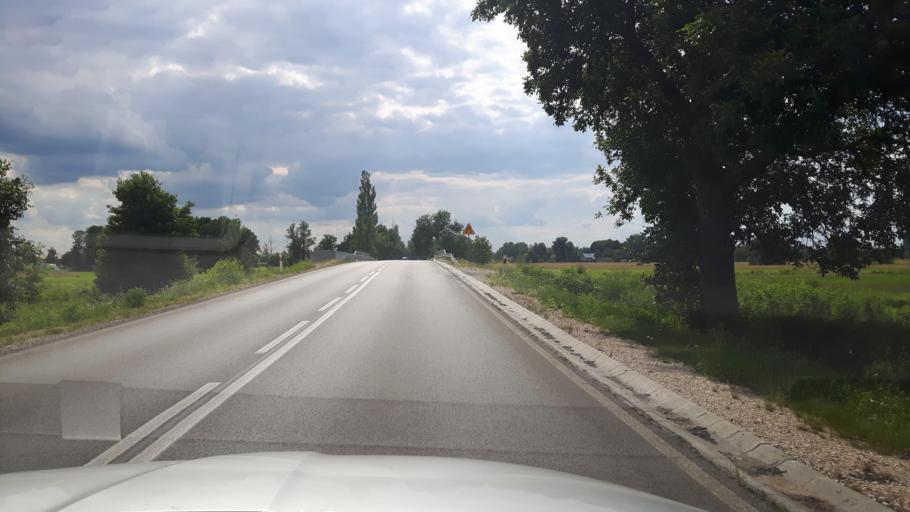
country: PL
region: Masovian Voivodeship
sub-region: Powiat wolominski
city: Ostrowek
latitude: 52.3771
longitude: 21.3523
